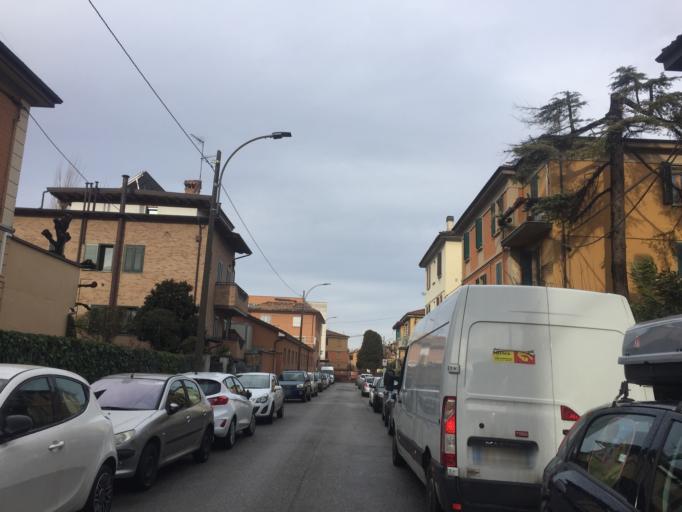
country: IT
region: Emilia-Romagna
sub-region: Provincia di Bologna
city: Casalecchio di Reno
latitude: 44.5050
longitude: 11.3005
